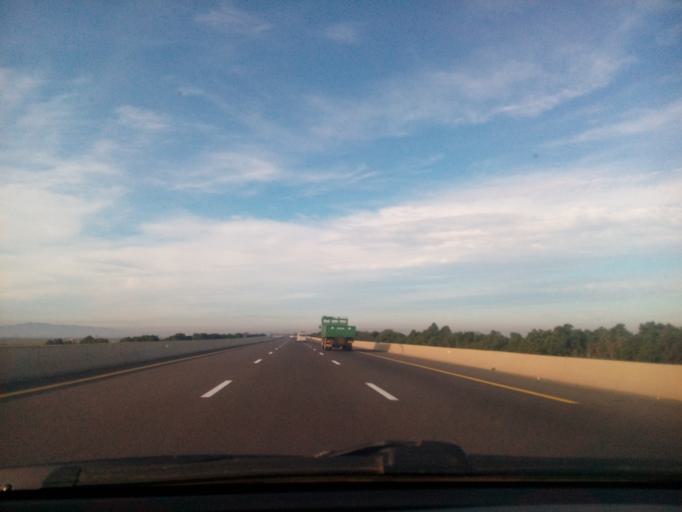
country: DZ
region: Mascara
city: Sig
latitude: 35.5909
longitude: -0.0636
